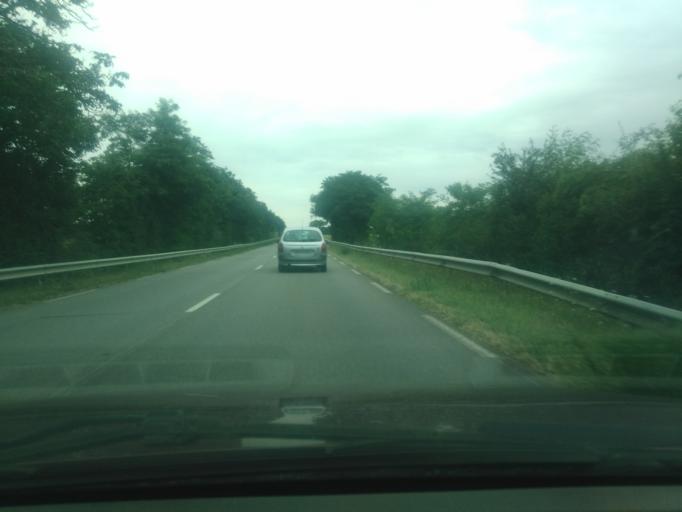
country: FR
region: Centre
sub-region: Departement de l'Indre
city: Le Blanc
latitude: 46.6070
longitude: 0.9923
